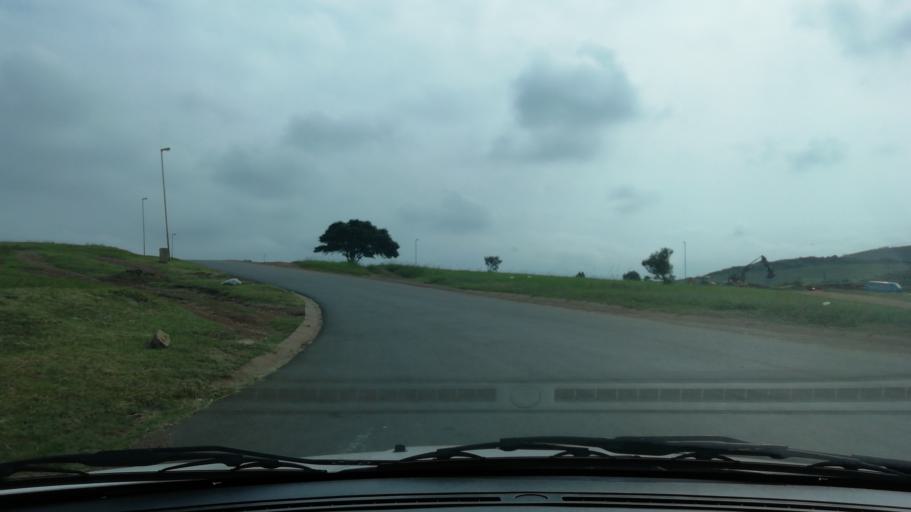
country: ZA
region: KwaZulu-Natal
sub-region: uThungulu District Municipality
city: Empangeni
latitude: -28.7430
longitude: 31.8828
